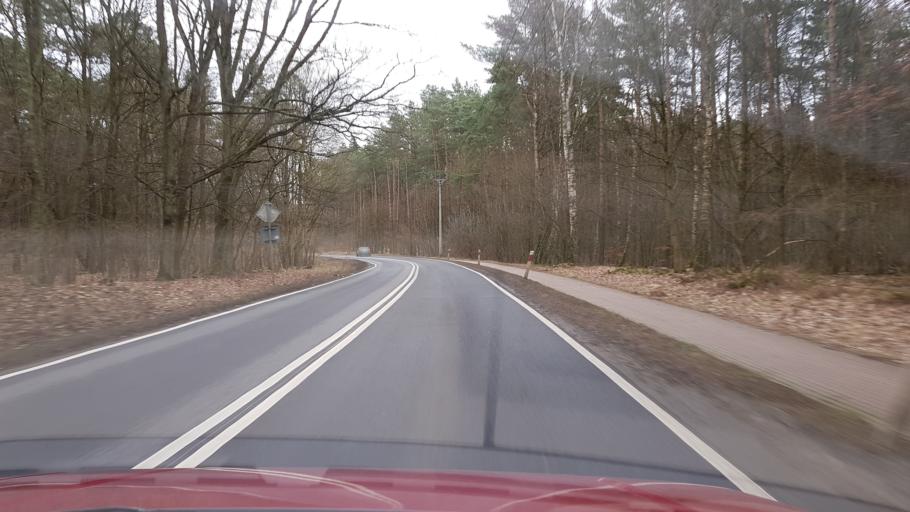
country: PL
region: West Pomeranian Voivodeship
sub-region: Powiat policki
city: Police
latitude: 53.5416
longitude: 14.4837
